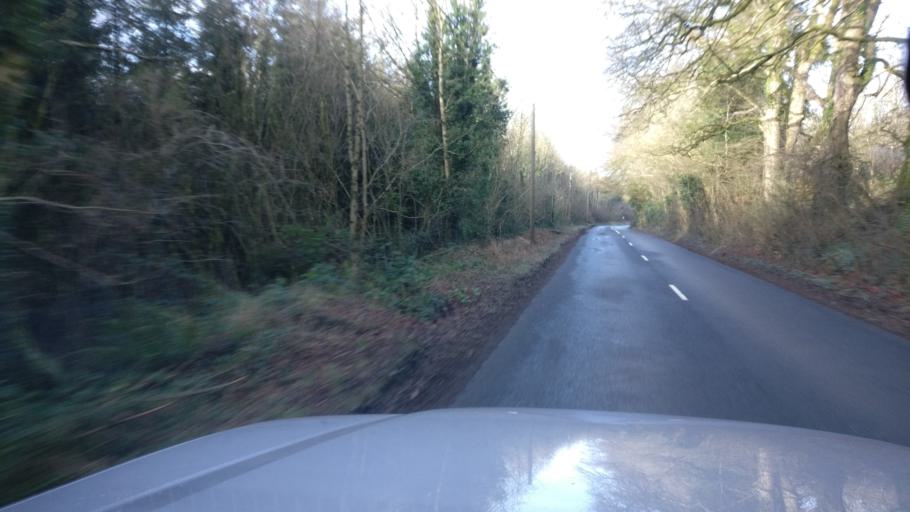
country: IE
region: Leinster
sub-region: Laois
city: Stradbally
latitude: 52.9424
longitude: -7.1996
